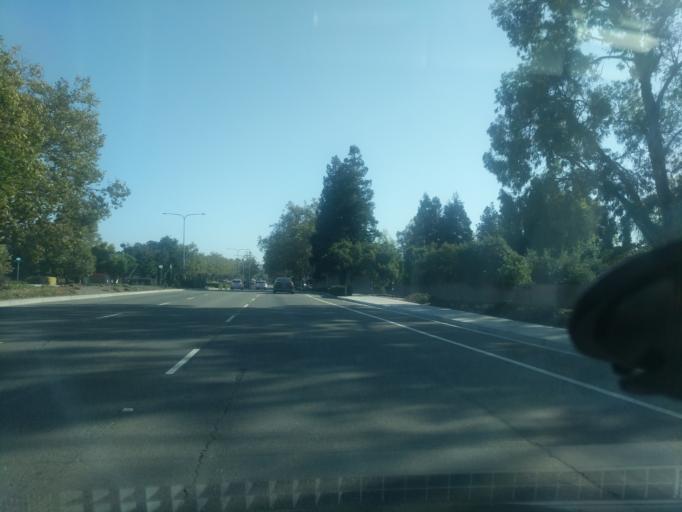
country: US
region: California
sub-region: Alameda County
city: Pleasanton
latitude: 37.6867
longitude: -121.8775
